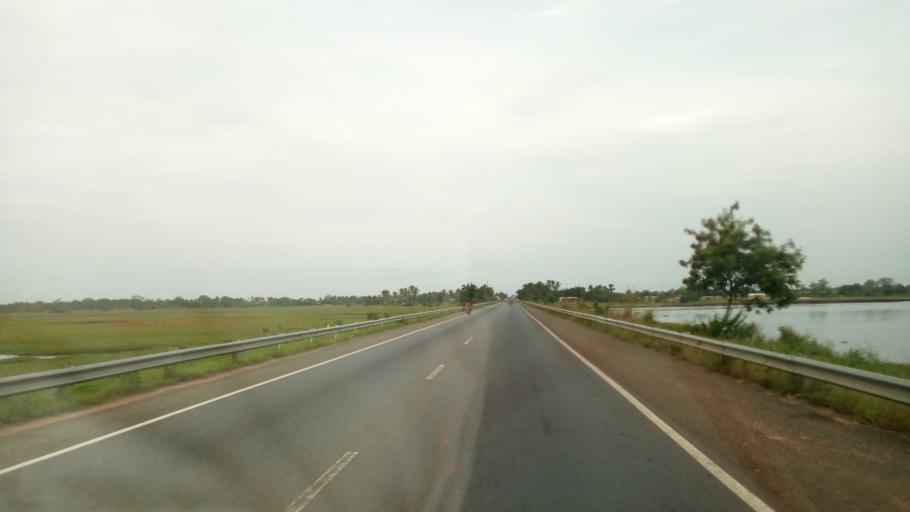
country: GH
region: Volta
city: Keta
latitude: 6.0697
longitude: 1.0236
